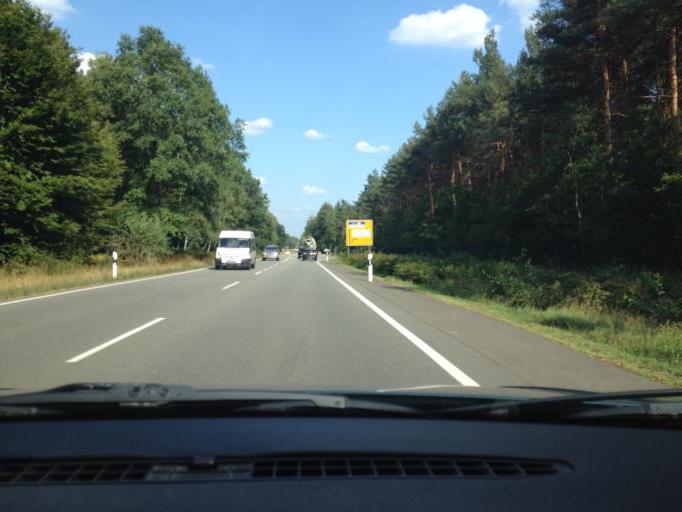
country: DE
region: Rheinland-Pfalz
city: Rodenbach
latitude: 49.4421
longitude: 7.6423
